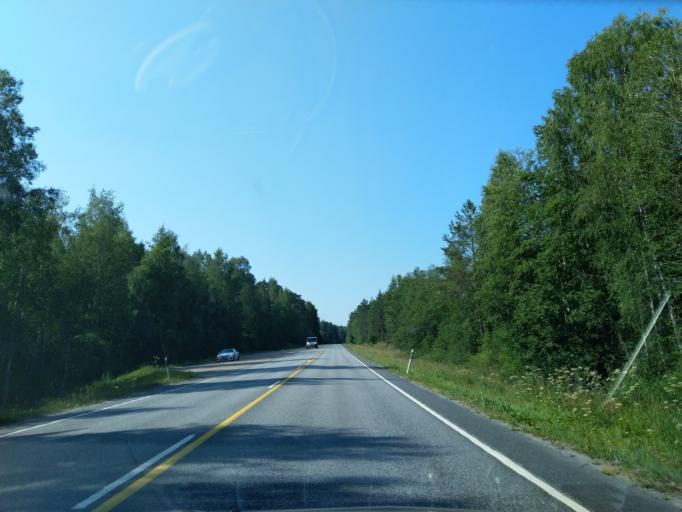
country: FI
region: Satakunta
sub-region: Pori
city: Noormarkku
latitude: 61.6056
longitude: 21.8811
